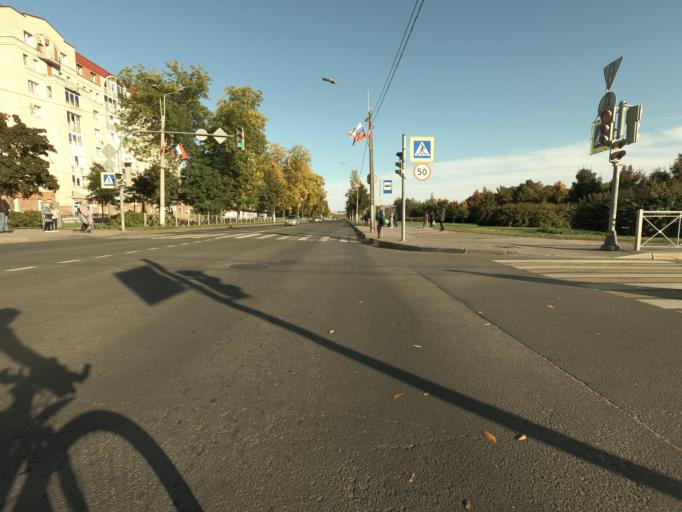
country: RU
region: St.-Petersburg
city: Kolpino
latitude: 59.7410
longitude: 30.5867
